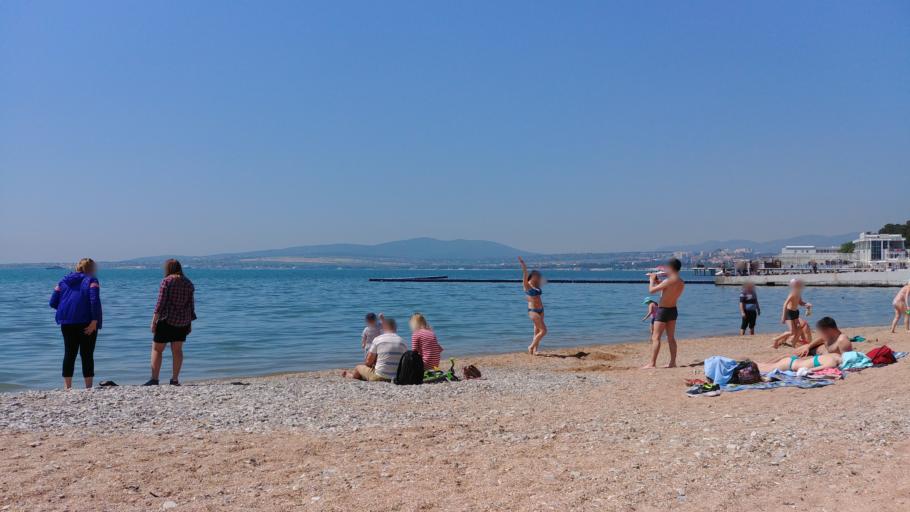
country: RU
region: Krasnodarskiy
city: Gelendzhik
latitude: 44.5638
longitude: 38.0766
